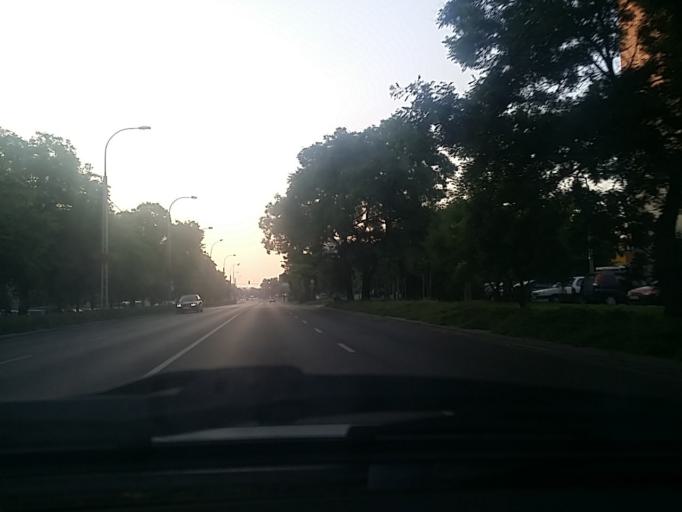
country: HU
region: Budapest
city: Budapest XVII. keruelet
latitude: 47.4805
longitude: 19.2520
